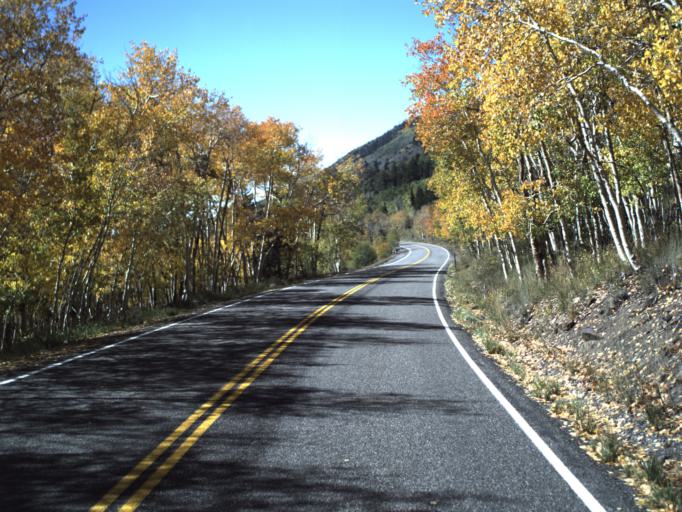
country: US
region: Utah
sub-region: Wayne County
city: Loa
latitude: 38.5408
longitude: -111.7329
